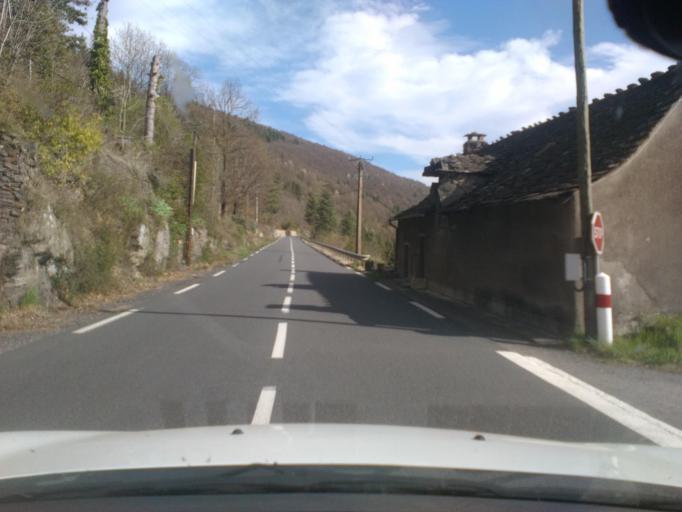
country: FR
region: Languedoc-Roussillon
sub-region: Departement de la Lozere
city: Florac
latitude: 44.3773
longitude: 3.5520
